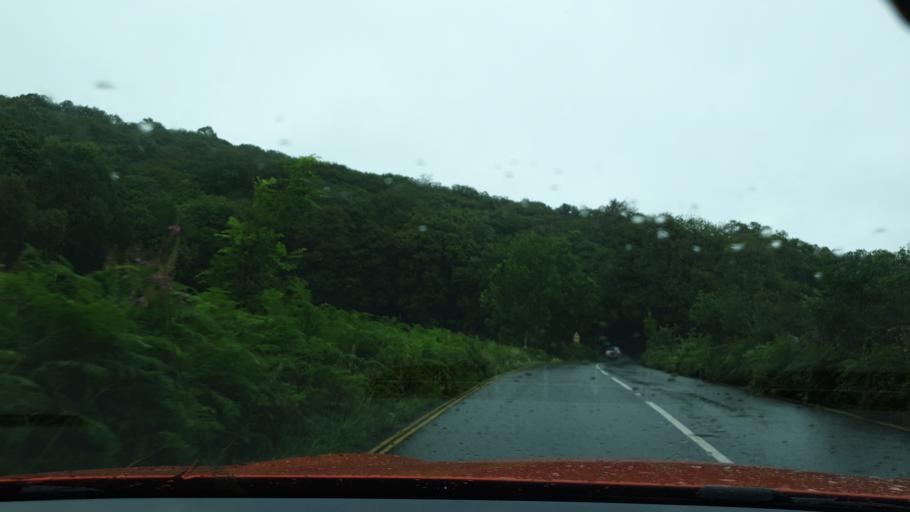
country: GB
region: England
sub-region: Cumbria
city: Ulverston
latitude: 54.3130
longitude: -3.0918
